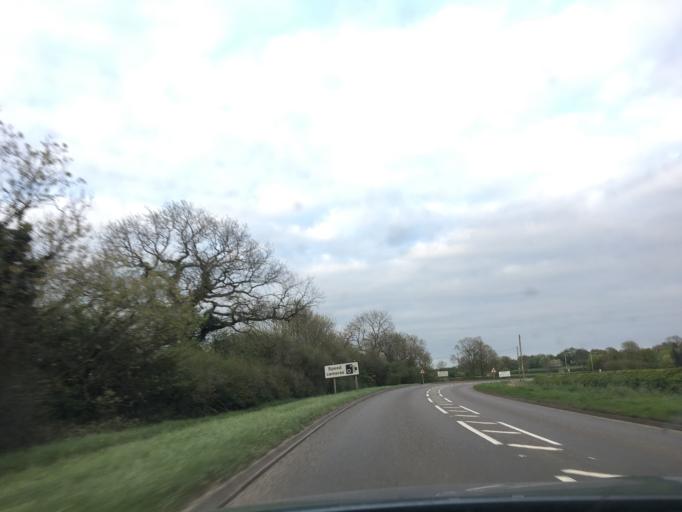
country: GB
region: England
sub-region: Leicestershire
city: Houghton on the Hill
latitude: 52.6299
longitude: -1.0067
